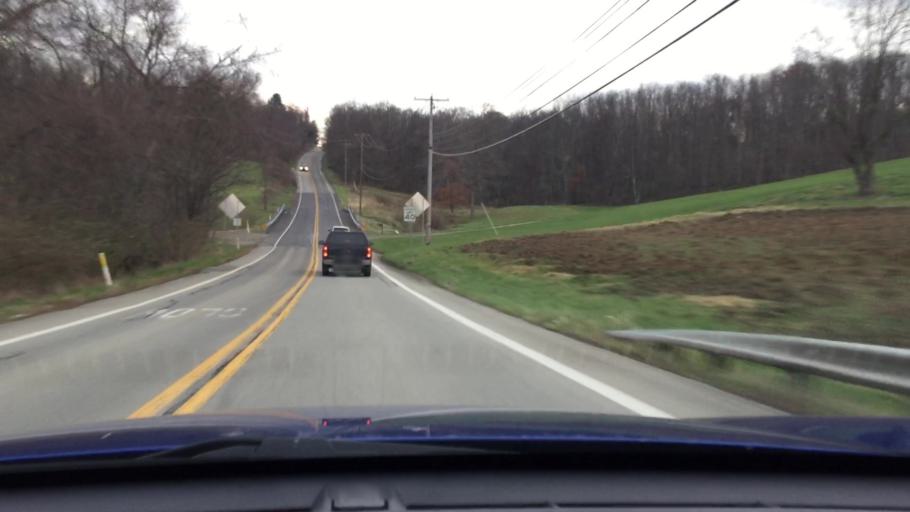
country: US
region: Pennsylvania
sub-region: Allegheny County
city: Elizabeth
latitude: 40.2399
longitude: -79.8595
